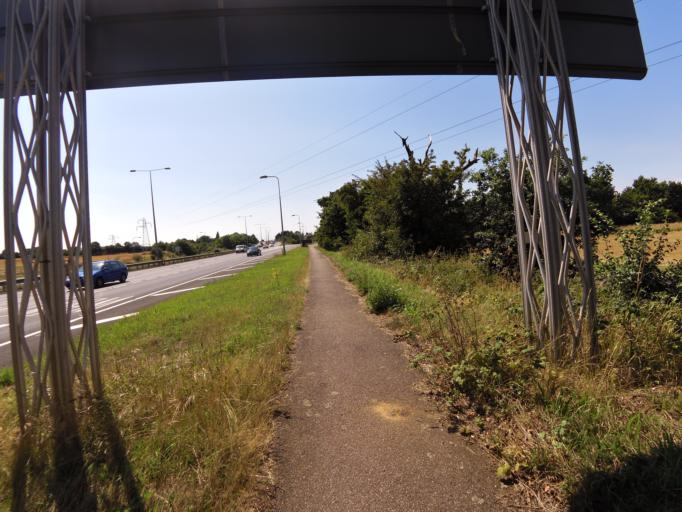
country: GB
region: England
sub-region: Suffolk
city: Capel Saint Mary
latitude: 52.0075
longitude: 1.0608
